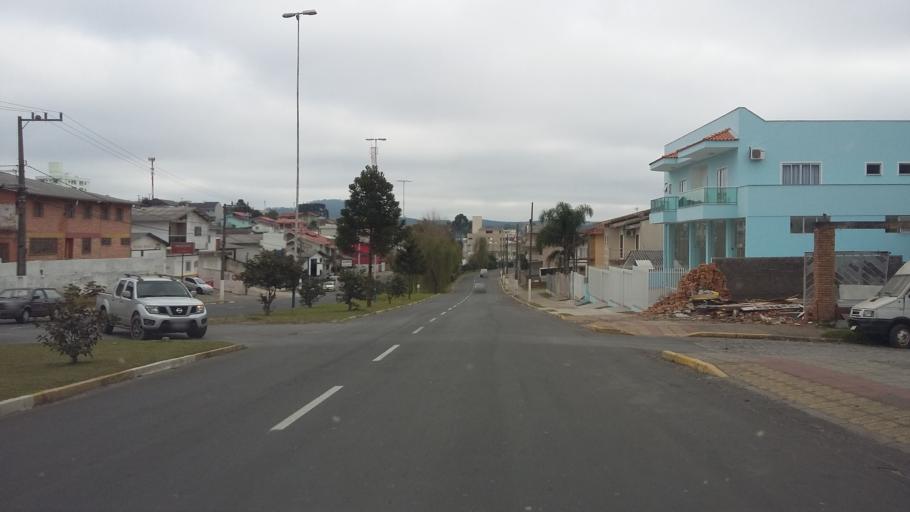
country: BR
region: Santa Catarina
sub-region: Lages
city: Lages
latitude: -27.8256
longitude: -50.3385
